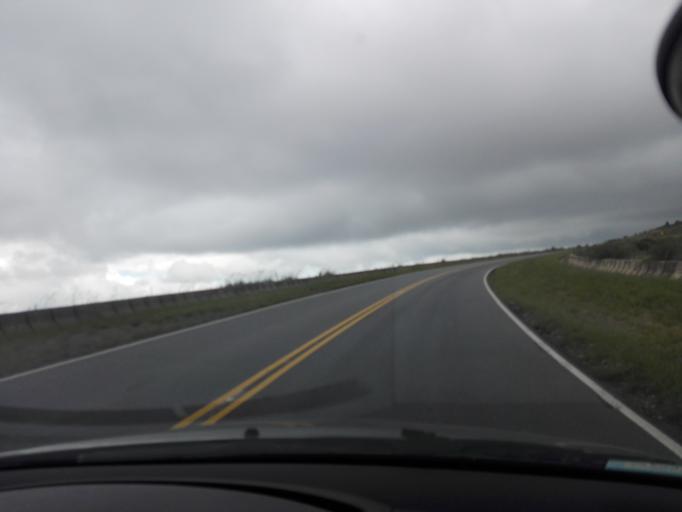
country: AR
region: Cordoba
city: Cuesta Blanca
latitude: -31.6164
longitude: -64.6700
